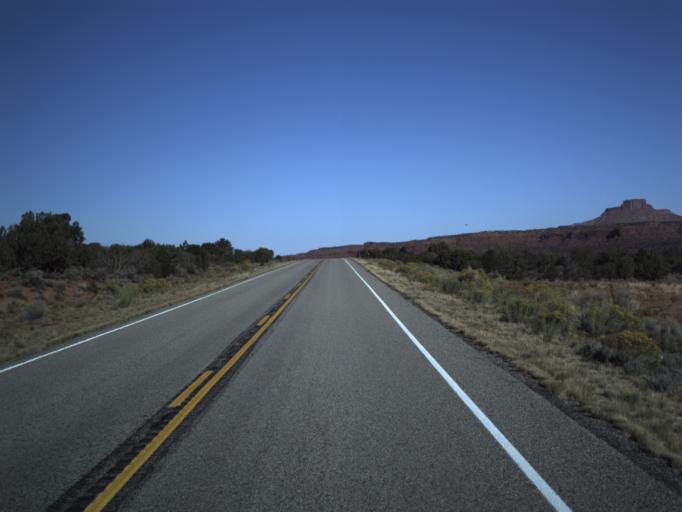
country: US
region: Utah
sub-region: San Juan County
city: Blanding
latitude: 37.6511
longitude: -110.1708
